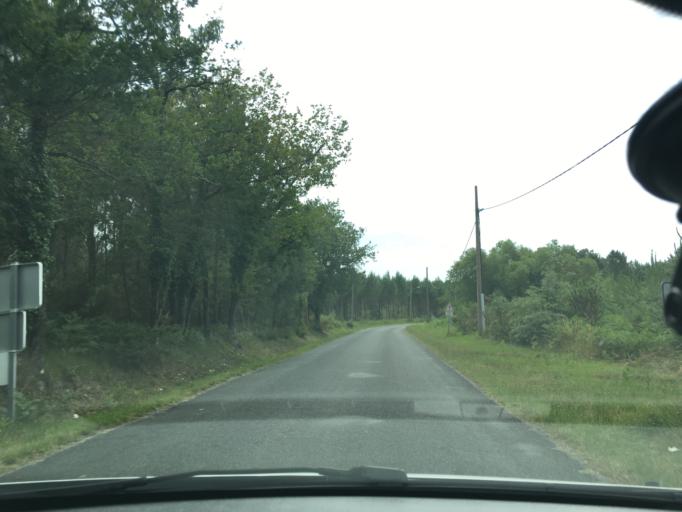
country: FR
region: Aquitaine
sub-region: Departement de la Gironde
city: Gaillan-en-Medoc
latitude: 45.3536
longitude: -1.0509
